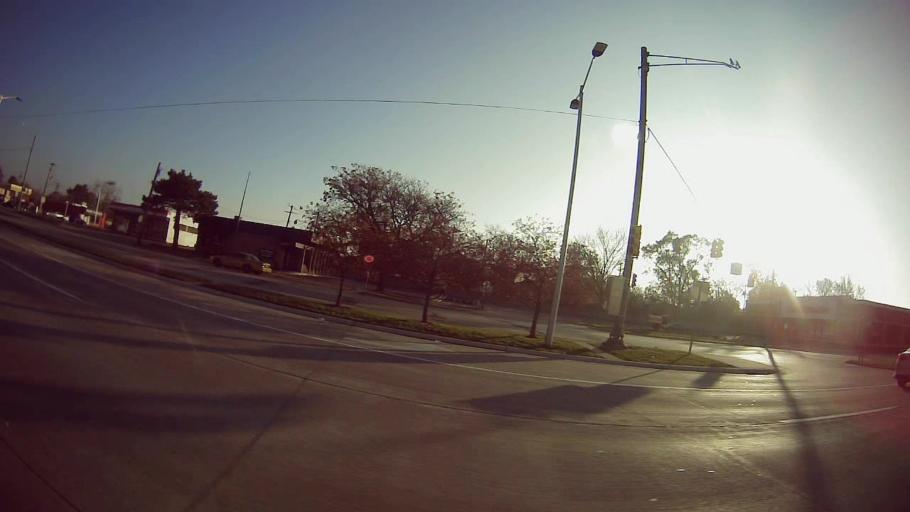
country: US
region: Michigan
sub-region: Oakland County
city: Oak Park
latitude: 42.4591
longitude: -83.2013
